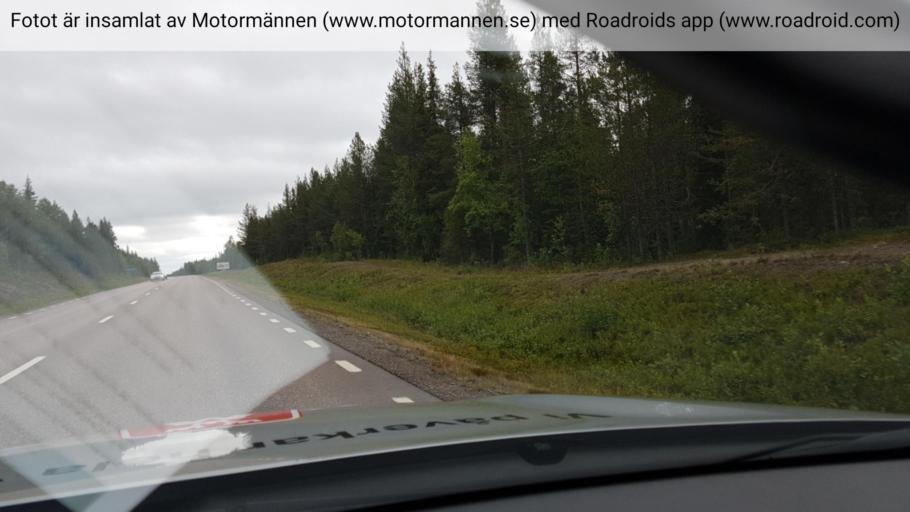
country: SE
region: Norrbotten
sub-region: Gallivare Kommun
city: Gaellivare
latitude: 67.0839
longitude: 21.0394
